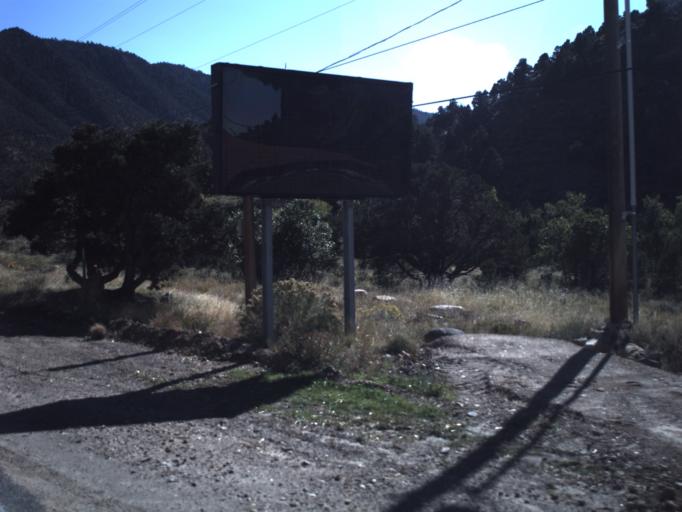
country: US
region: Utah
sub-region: Iron County
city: Parowan
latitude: 37.8298
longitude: -112.8149
